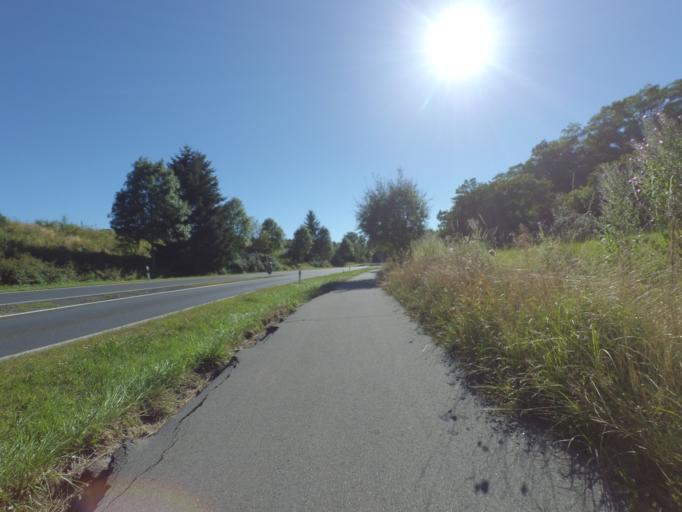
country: DE
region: Rheinland-Pfalz
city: Daun
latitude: 50.2081
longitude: 6.8410
